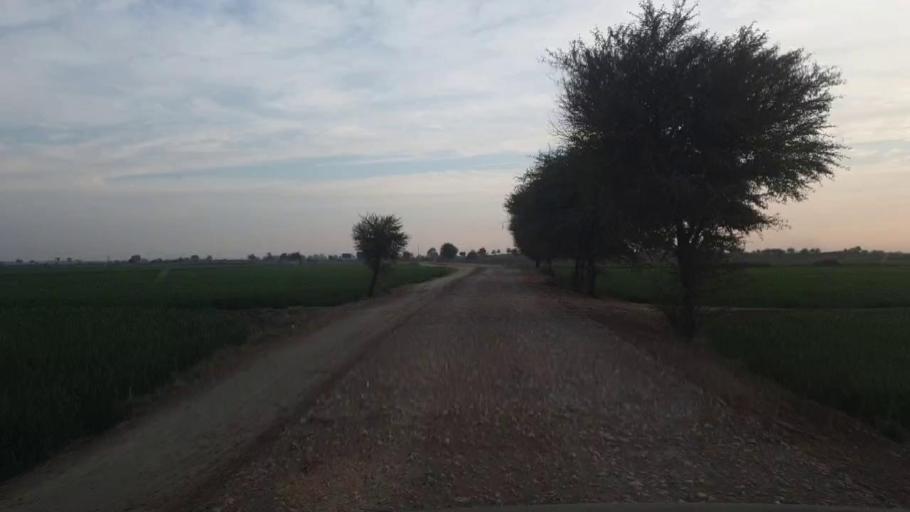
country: PK
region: Sindh
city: Shahpur Chakar
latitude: 26.0622
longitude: 68.5282
